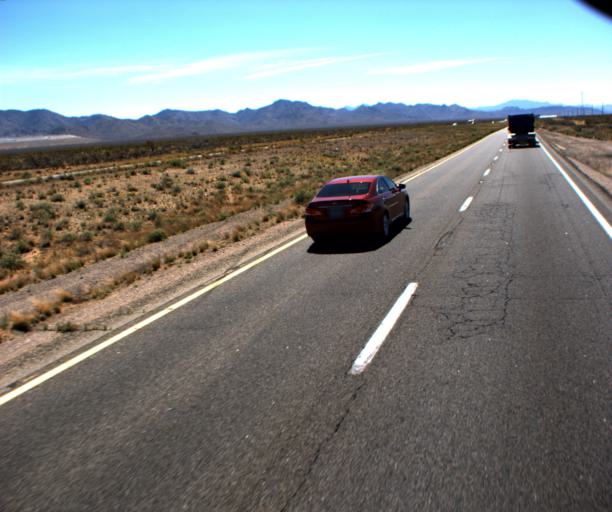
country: US
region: Arizona
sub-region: Mohave County
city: Golden Valley
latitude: 35.3494
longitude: -114.2252
